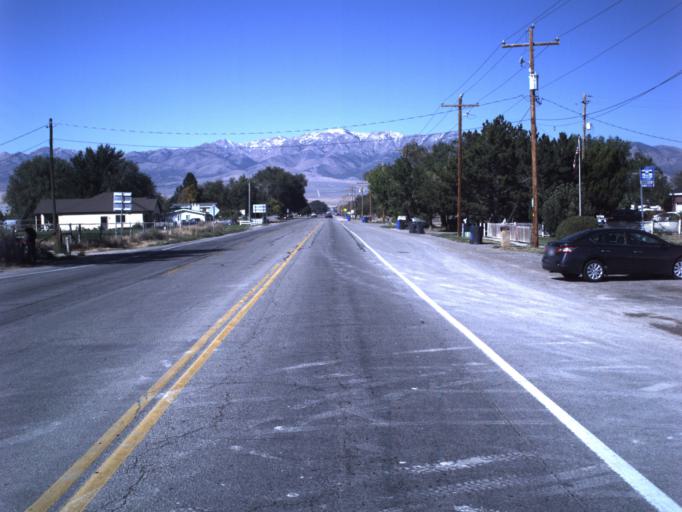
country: US
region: Utah
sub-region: Tooele County
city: Grantsville
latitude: 40.5996
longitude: -112.4265
